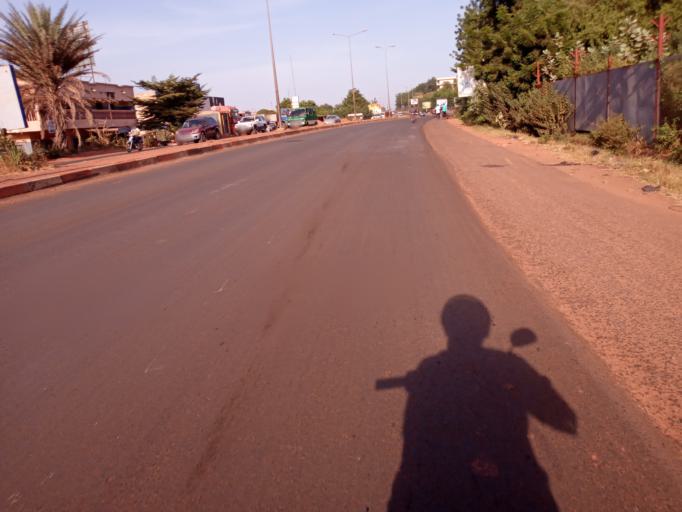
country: ML
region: Bamako
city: Bamako
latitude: 12.6153
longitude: -7.9900
